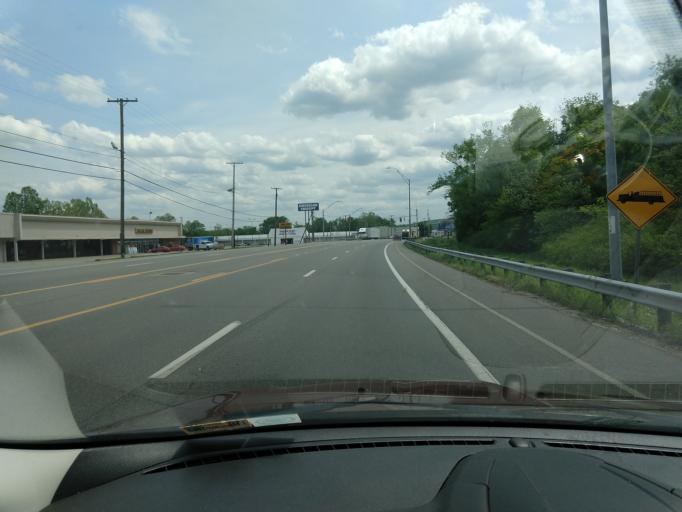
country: US
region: West Virginia
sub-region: Kanawha County
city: Dunbar
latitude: 38.3699
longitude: -81.7679
